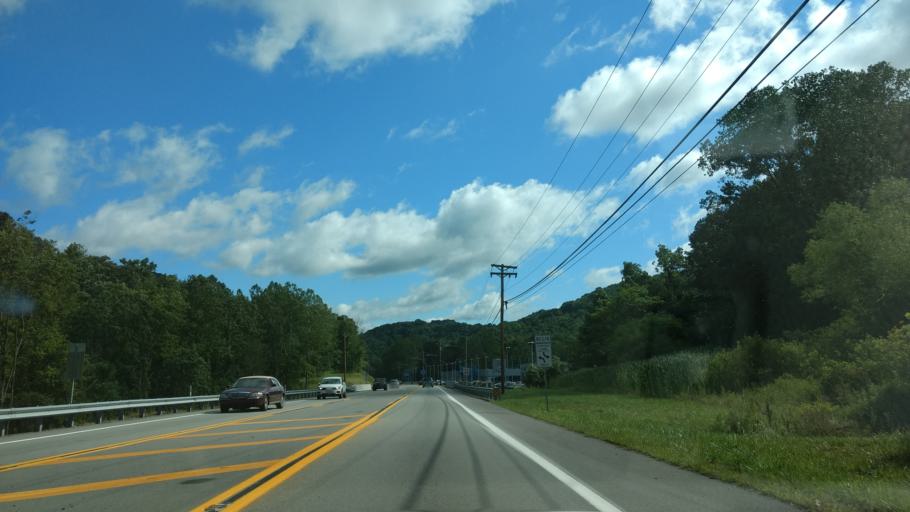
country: US
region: Pennsylvania
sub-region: Westmoreland County
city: Murrysville
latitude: 40.4296
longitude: -79.7190
